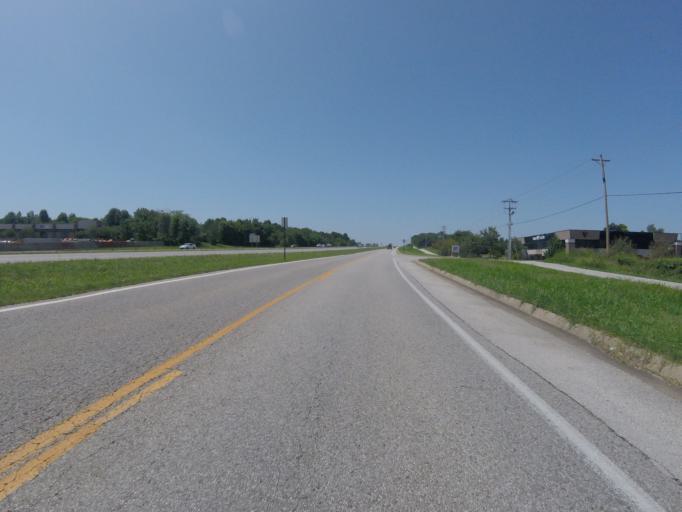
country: US
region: Arkansas
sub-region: Washington County
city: Johnson
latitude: 36.1033
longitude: -94.1827
